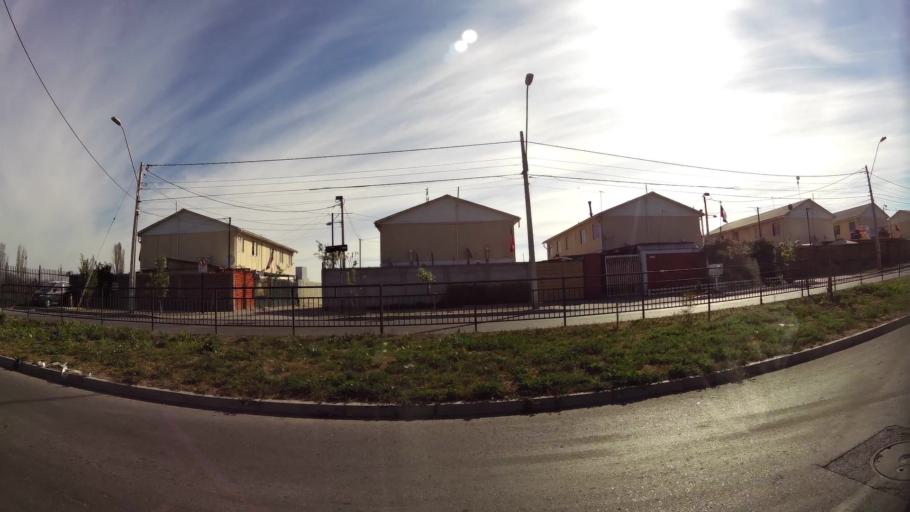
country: CL
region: Santiago Metropolitan
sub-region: Provincia de Cordillera
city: Puente Alto
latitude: -33.6303
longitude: -70.5962
